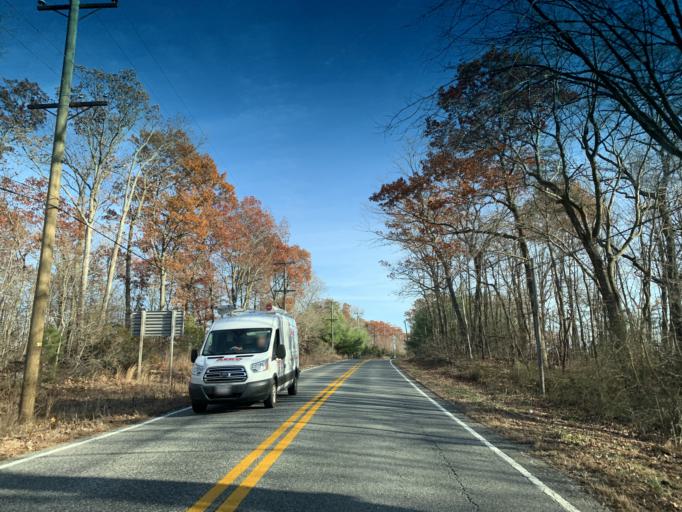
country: US
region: Maryland
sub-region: Cecil County
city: Charlestown
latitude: 39.5839
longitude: -76.0118
